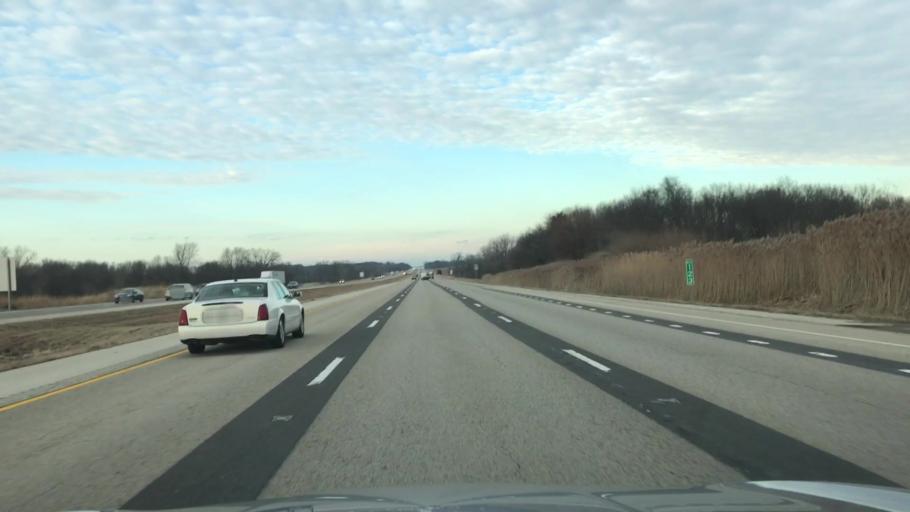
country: US
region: Illinois
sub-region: Logan County
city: Lincoln
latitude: 40.1181
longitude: -89.4165
